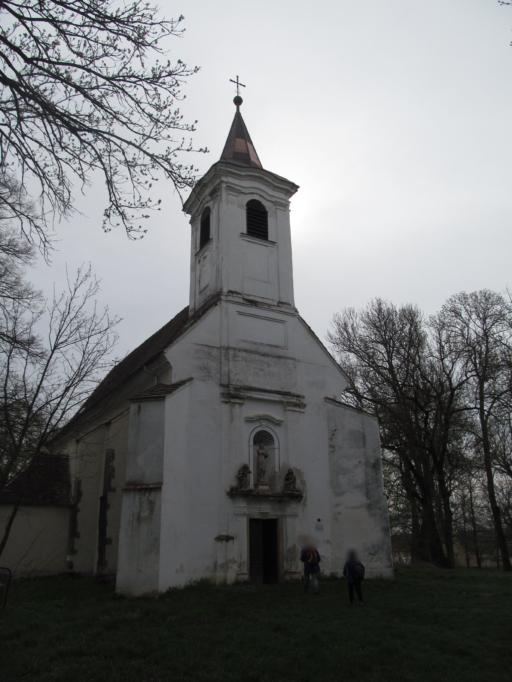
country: HU
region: Veszprem
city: Urkut
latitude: 46.9885
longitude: 17.7027
